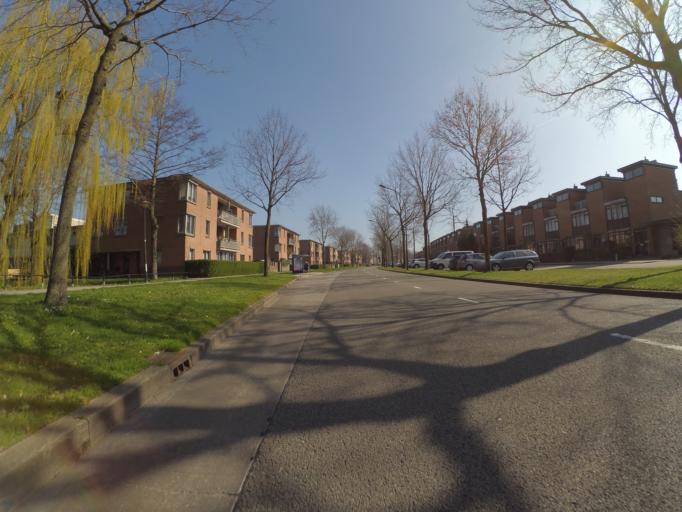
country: NL
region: Utrecht
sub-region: Gemeente Amersfoort
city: Hoogland
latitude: 52.2035
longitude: 5.3793
